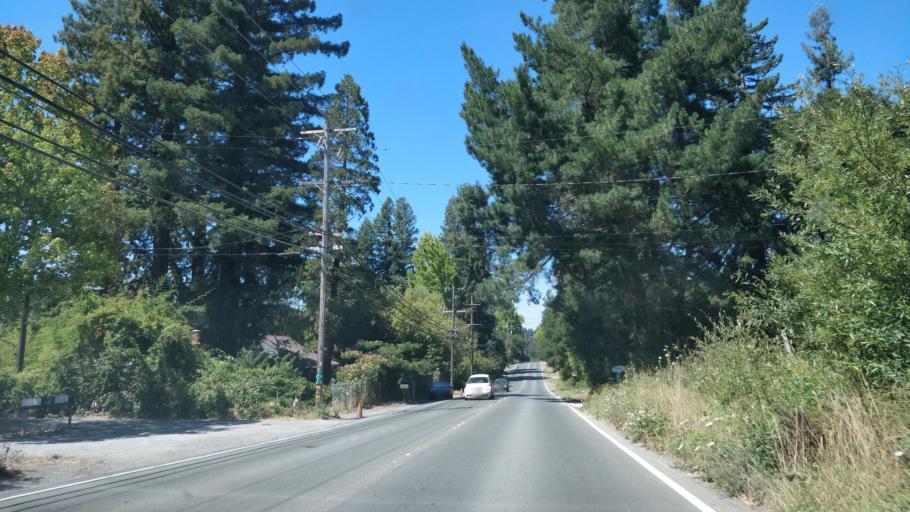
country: US
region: California
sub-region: Sonoma County
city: Forestville
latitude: 38.4824
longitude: -122.8949
